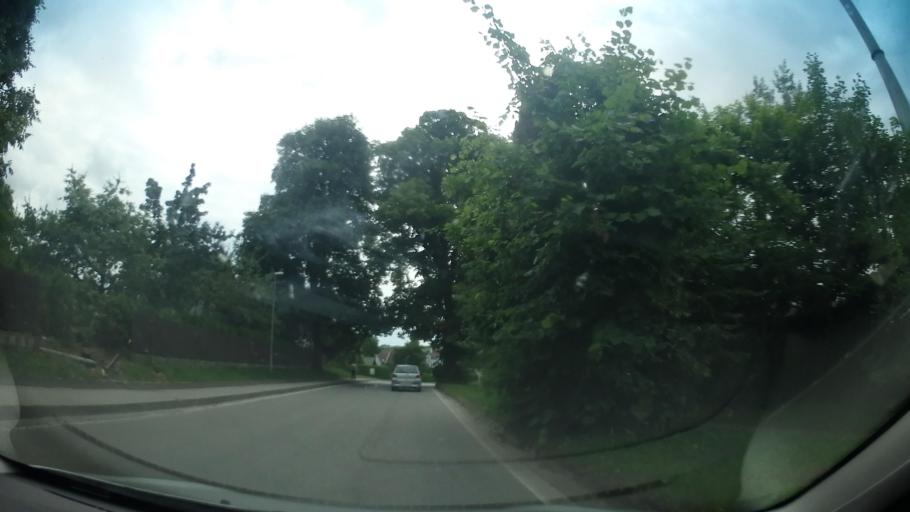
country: CZ
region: Vysocina
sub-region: Okres Zd'ar nad Sazavou
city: Nove Mesto na Morave
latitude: 49.5708
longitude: 16.0786
